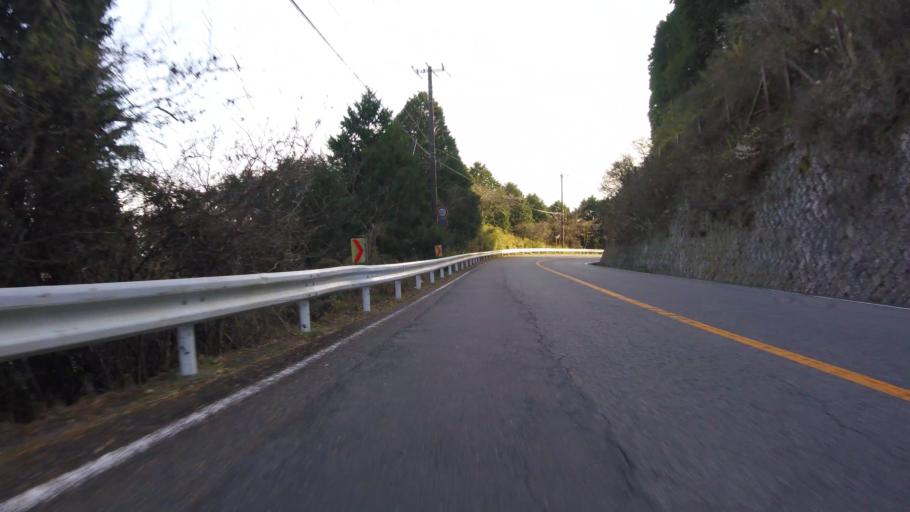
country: JP
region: Shizuoka
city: Atami
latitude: 35.1179
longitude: 139.0431
